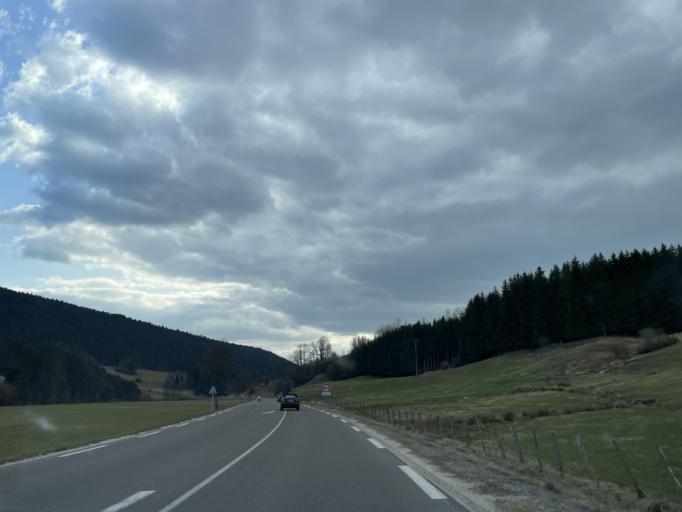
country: FR
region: Franche-Comte
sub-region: Departement du Doubs
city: Gilley
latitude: 47.0001
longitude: 6.4745
